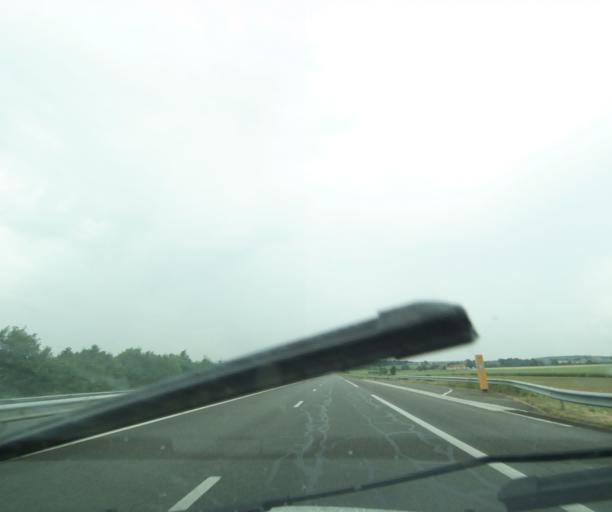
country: FR
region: Auvergne
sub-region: Departement de l'Allier
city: Vallon-en-Sully
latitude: 46.5444
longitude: 2.5533
